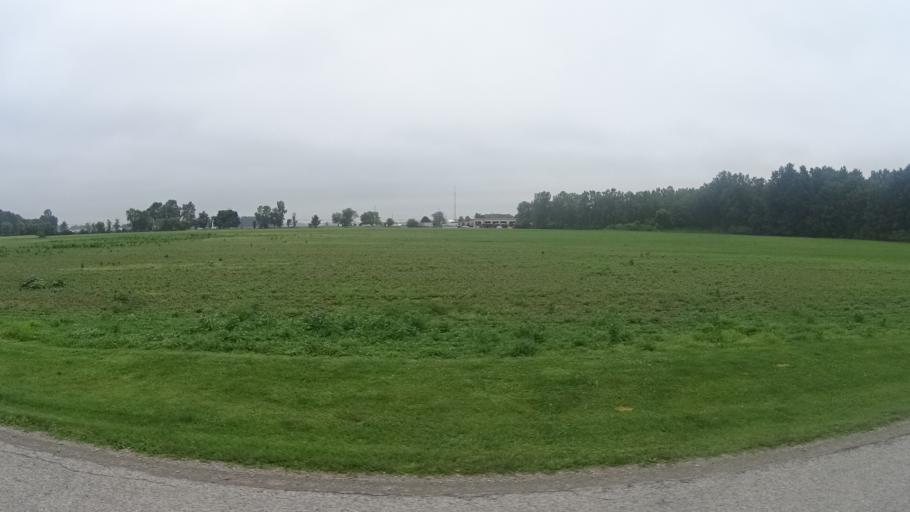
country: US
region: Ohio
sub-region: Erie County
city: Milan
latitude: 41.3141
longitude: -82.6036
